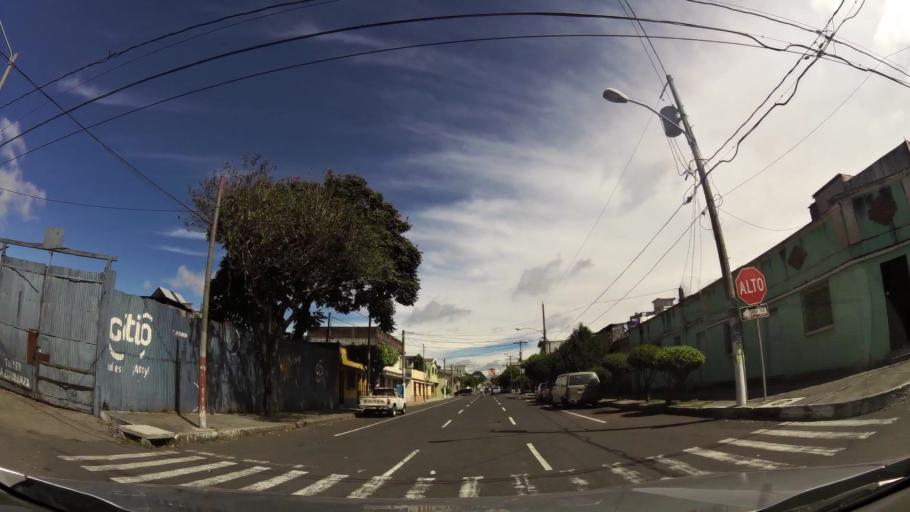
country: GT
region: Guatemala
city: Guatemala City
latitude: 14.5999
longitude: -90.5440
